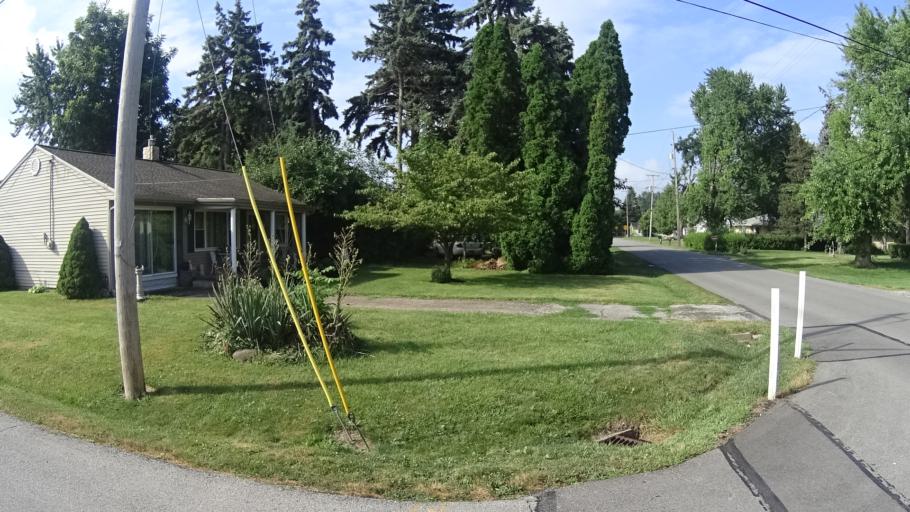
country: US
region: Ohio
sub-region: Erie County
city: Sandusky
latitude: 41.4381
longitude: -82.6759
